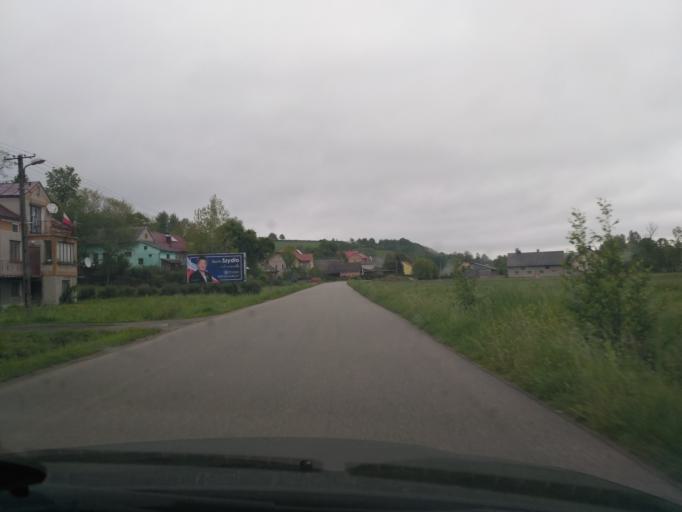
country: PL
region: Subcarpathian Voivodeship
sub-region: Powiat debicki
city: Jodlowa
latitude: 49.8741
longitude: 21.2651
